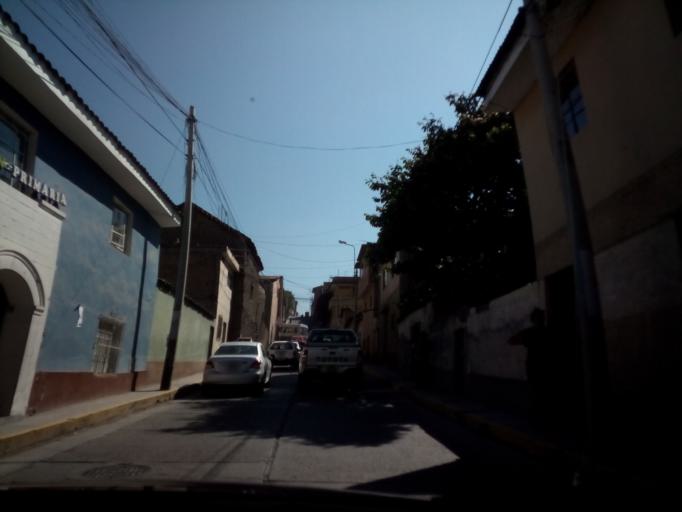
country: PE
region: Ayacucho
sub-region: Provincia de Huamanga
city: Ayacucho
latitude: -13.1625
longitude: -74.2220
